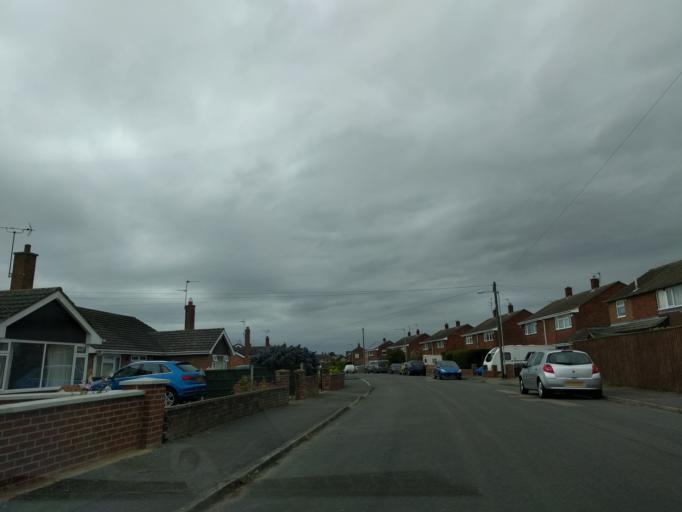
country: GB
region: England
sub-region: Nottinghamshire
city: Newark on Trent
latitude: 53.0509
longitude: -0.7837
